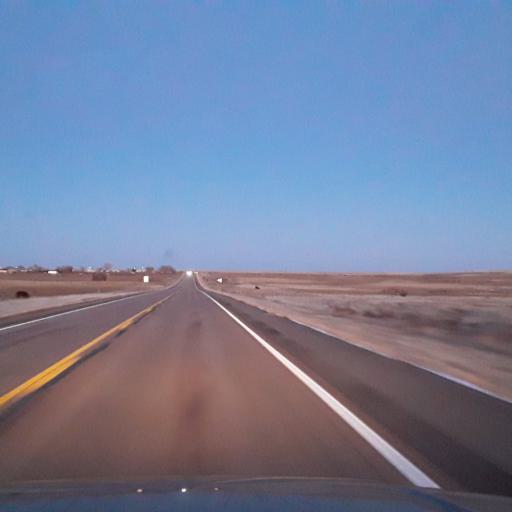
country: US
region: New Mexico
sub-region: Guadalupe County
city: Santa Rosa
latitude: 34.7755
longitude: -104.9547
